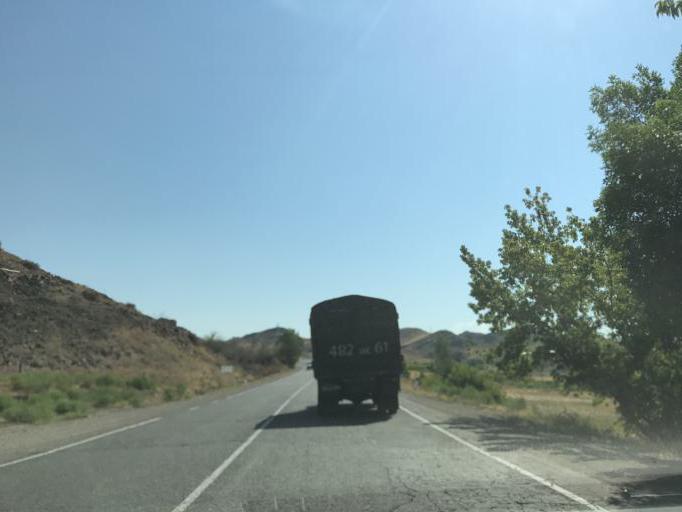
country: AM
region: Vayots' Dzori Marz
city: Getap'
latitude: 39.7486
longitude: 45.3172
